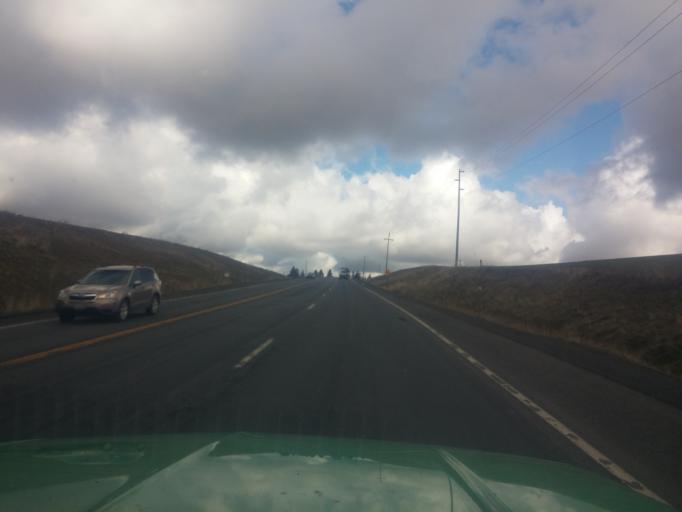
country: US
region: Idaho
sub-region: Latah County
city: Moscow
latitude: 46.8668
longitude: -117.0095
